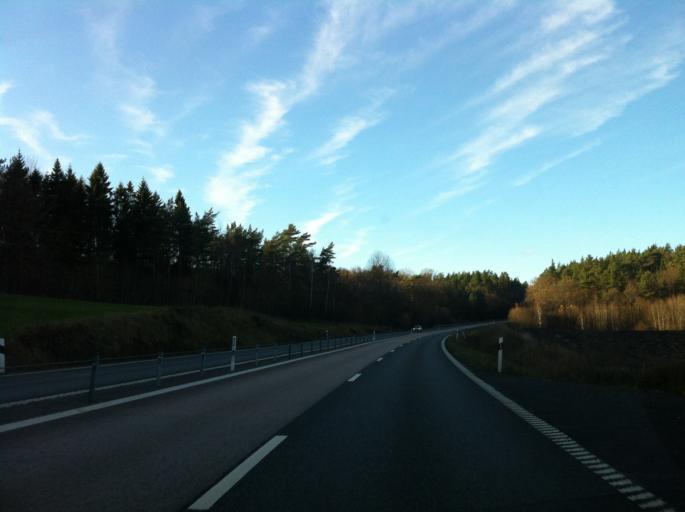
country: SE
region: Blekinge
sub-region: Karlshamns Kommun
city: Karlshamn
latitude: 56.1875
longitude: 14.9070
